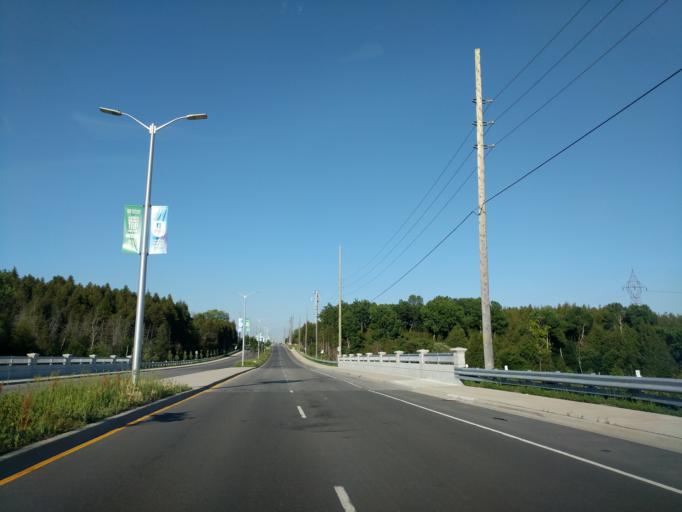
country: CA
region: Ontario
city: Oshawa
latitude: 43.9462
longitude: -78.9042
